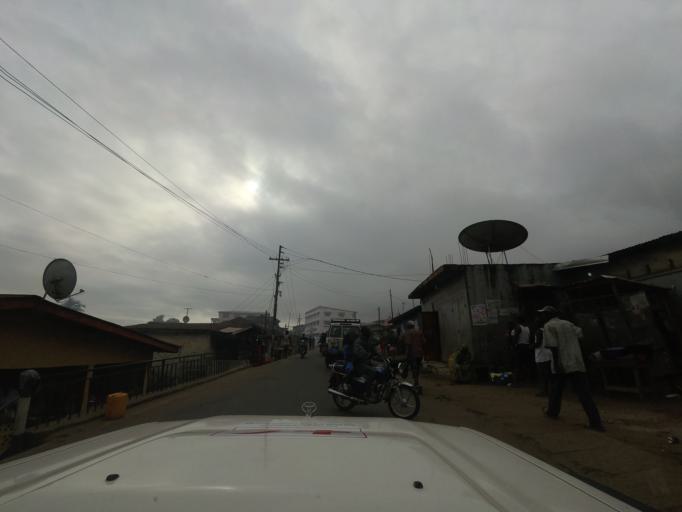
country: SL
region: Western Area
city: Freetown
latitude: 8.4843
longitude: -13.2477
